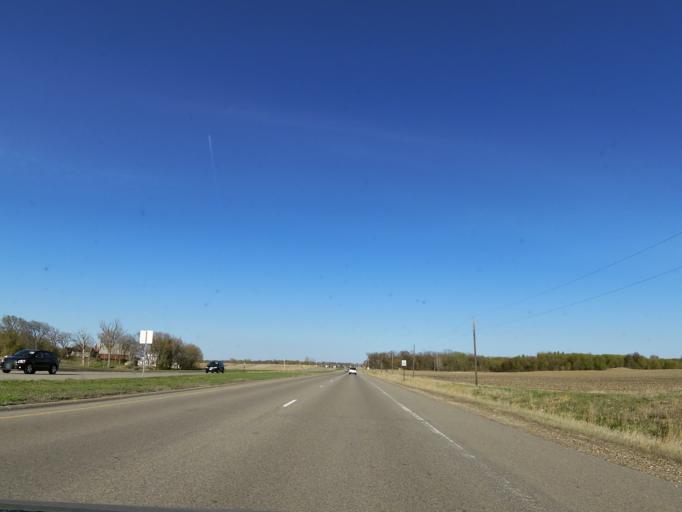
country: US
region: Minnesota
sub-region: Scott County
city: Elko New Market
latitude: 44.5730
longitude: -93.3279
